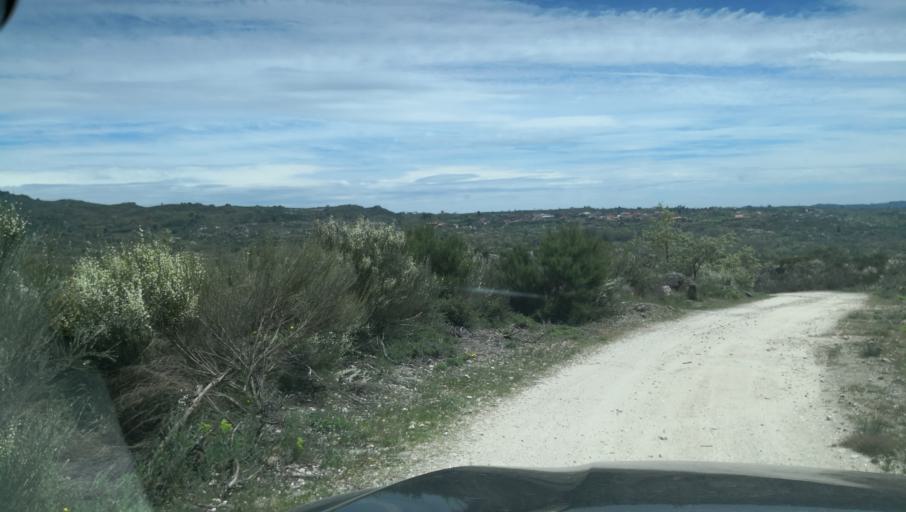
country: PT
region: Vila Real
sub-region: Vila Real
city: Vila Real
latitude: 41.3814
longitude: -7.6645
